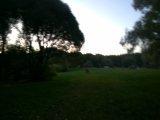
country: RU
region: Moscow
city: Pokrovskoye-Streshnevo
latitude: 55.8175
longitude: 37.4807
